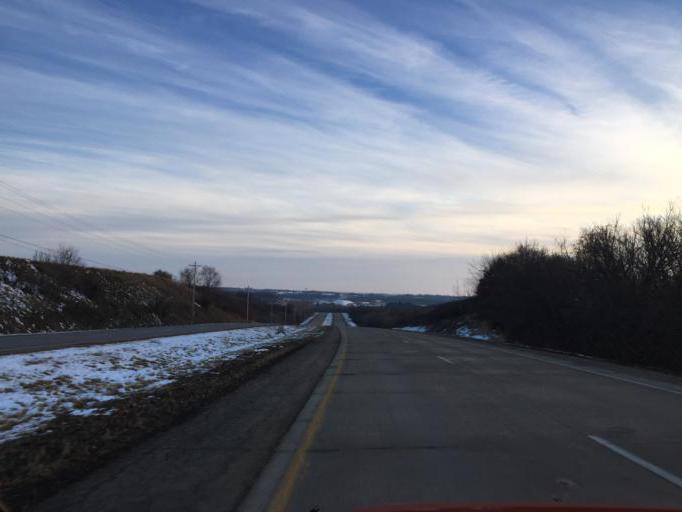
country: US
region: Minnesota
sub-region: Olmsted County
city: Rochester
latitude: 44.0449
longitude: -92.4291
